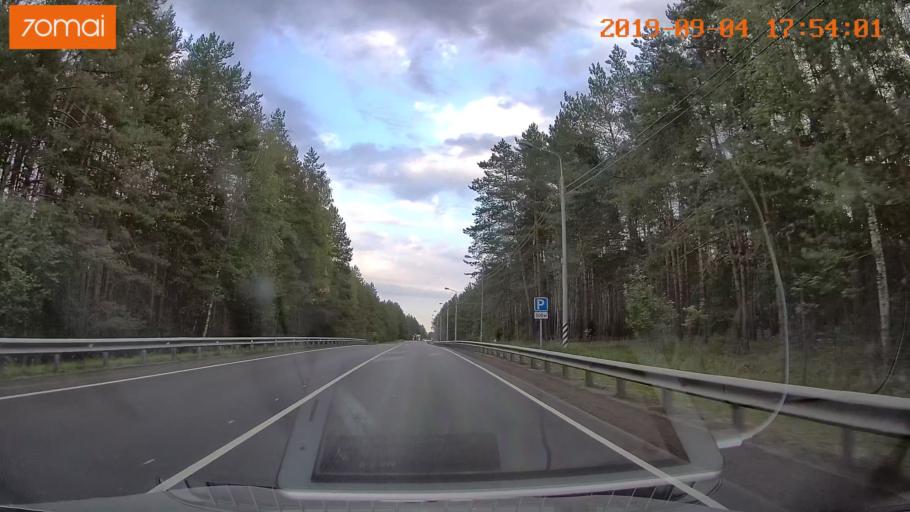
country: RU
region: Moskovskaya
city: Imeni Tsyurupy
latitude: 55.5129
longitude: 38.7343
